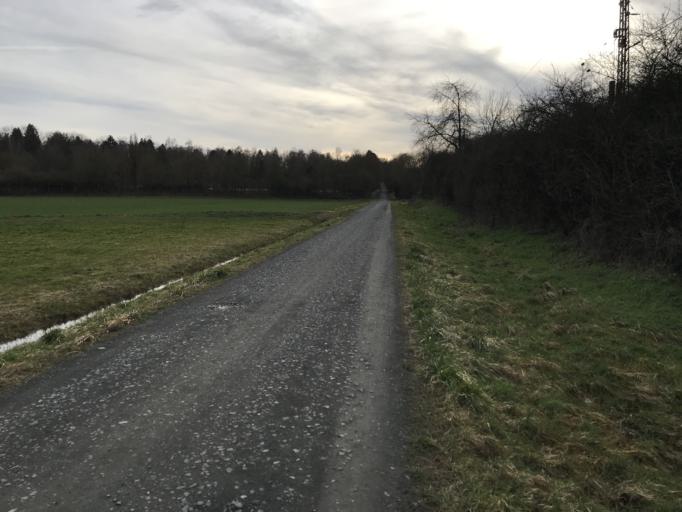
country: DE
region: Hesse
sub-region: Regierungsbezirk Giessen
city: Giessen
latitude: 50.6066
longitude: 8.6808
